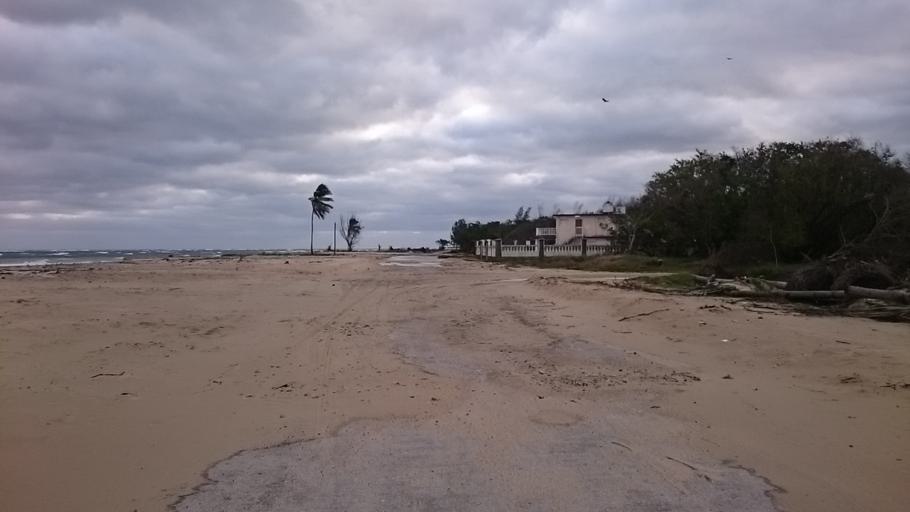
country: CU
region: Mayabeque
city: Jaruco
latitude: 23.1737
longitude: -82.1103
